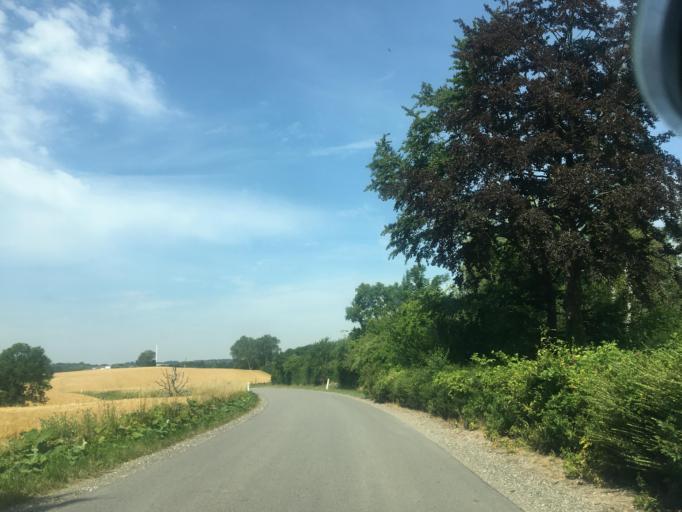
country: DK
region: Zealand
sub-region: Faxe Kommune
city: Ronnede
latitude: 55.2073
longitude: 12.0035
